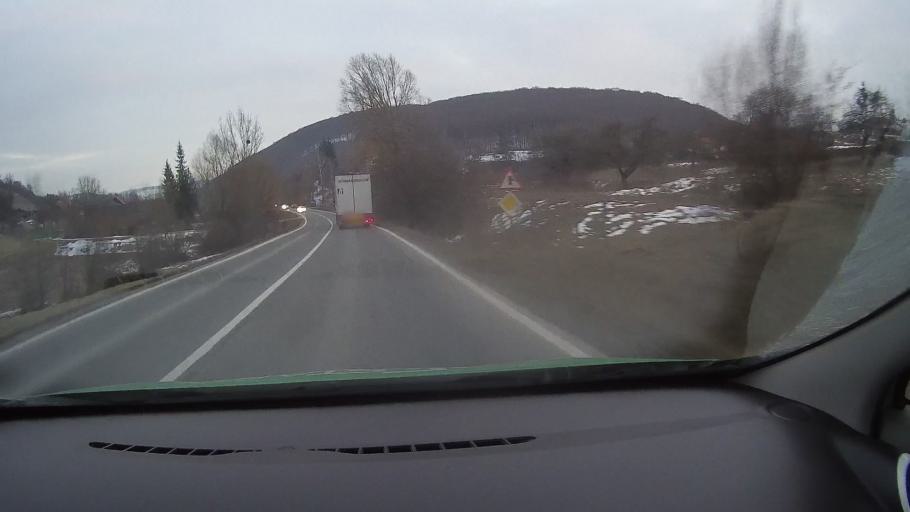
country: RO
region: Harghita
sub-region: Municipiul Odorheiu Secuiesc
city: Odorheiu Secuiesc
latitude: 46.3370
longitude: 25.2700
